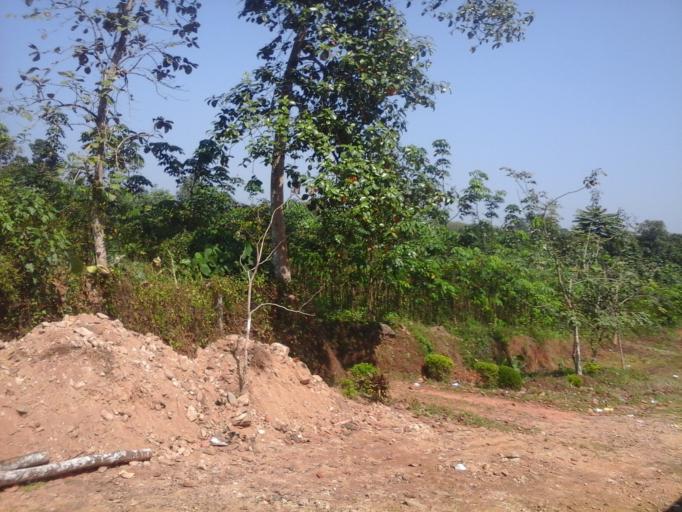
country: IN
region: Kerala
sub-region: Kottayam
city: Lalam
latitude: 9.6991
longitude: 76.7300
